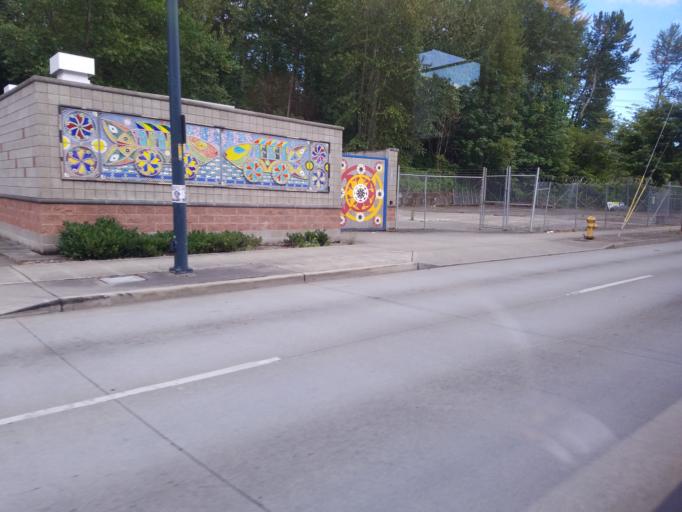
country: US
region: Washington
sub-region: King County
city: Riverton
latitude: 47.5214
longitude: -122.2796
